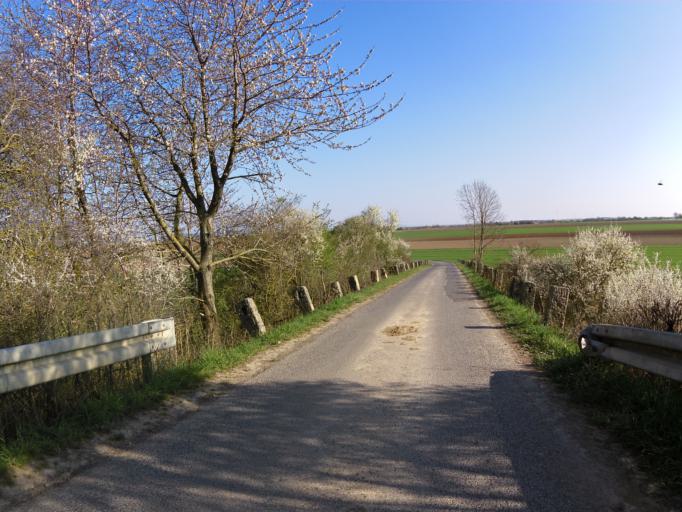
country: DE
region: Bavaria
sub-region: Regierungsbezirk Unterfranken
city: Oberpleichfeld
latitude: 49.8340
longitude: 10.0931
